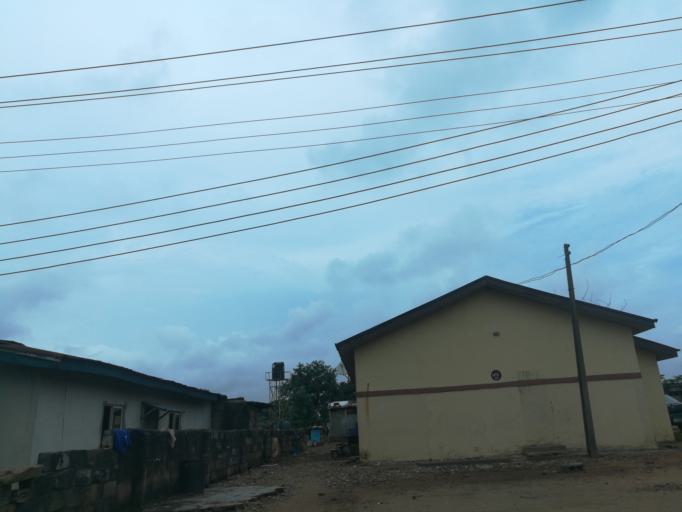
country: NG
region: Lagos
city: Oshodi
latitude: 6.5672
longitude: 3.3504
